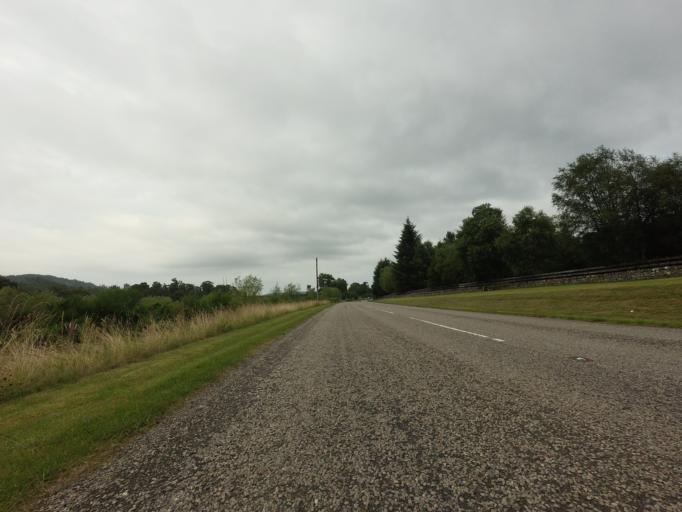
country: GB
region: Scotland
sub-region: Highland
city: Evanton
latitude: 57.9209
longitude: -4.3985
